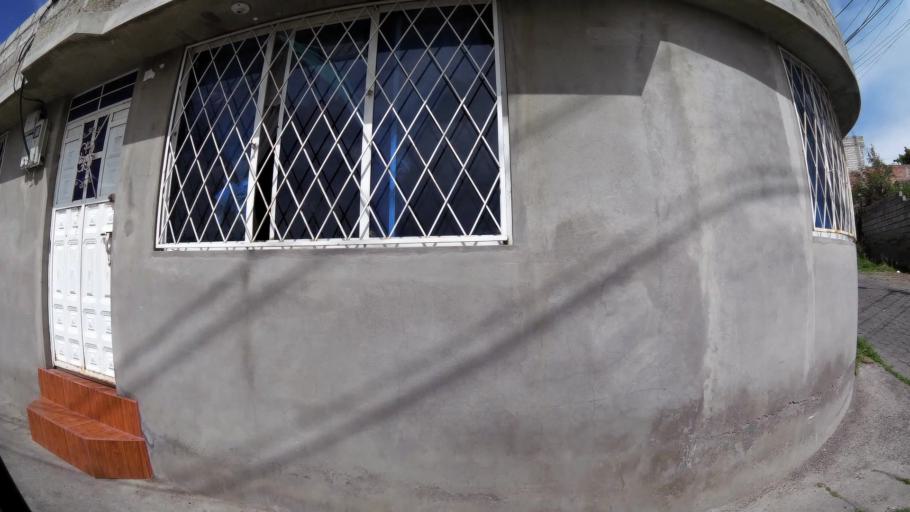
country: EC
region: Cotopaxi
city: Latacunga
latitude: -0.9326
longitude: -78.6084
